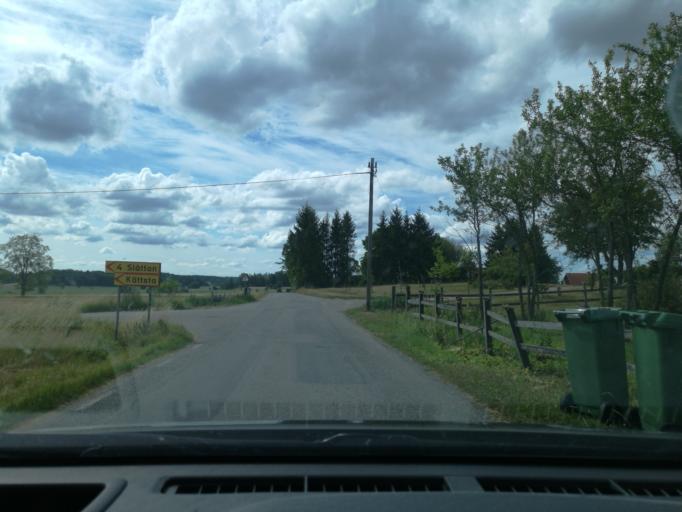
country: SE
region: Stockholm
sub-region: Sigtuna Kommun
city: Marsta
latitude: 59.6477
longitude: 17.8860
